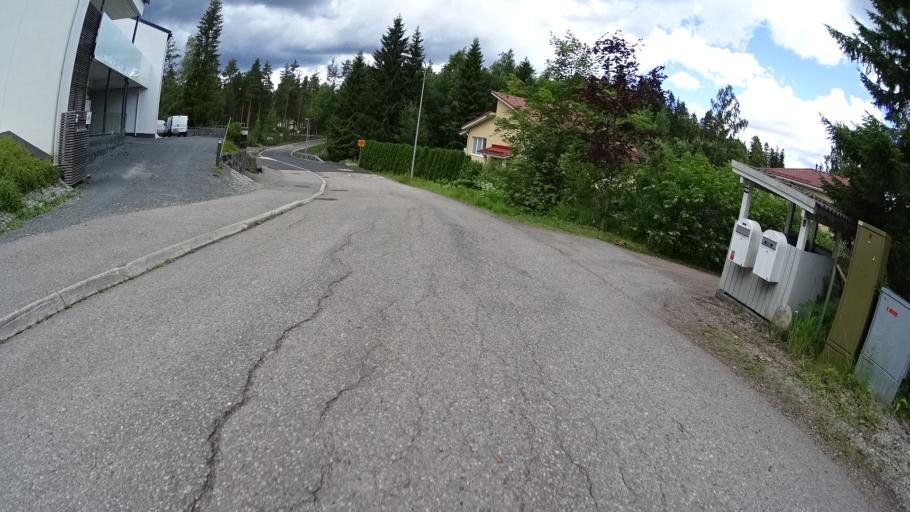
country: FI
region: Uusimaa
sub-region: Helsinki
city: Kauniainen
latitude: 60.2197
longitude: 24.7367
